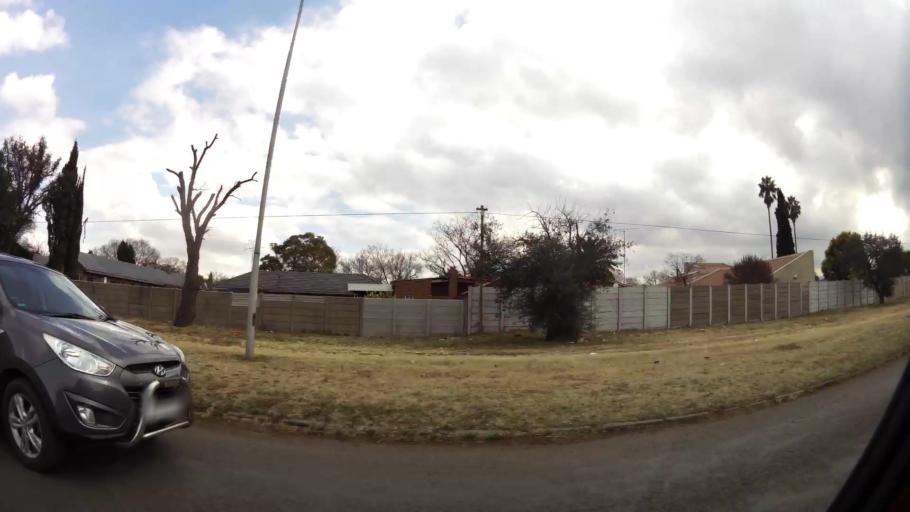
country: ZA
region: Gauteng
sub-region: Sedibeng District Municipality
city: Vanderbijlpark
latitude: -26.7091
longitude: 27.8359
